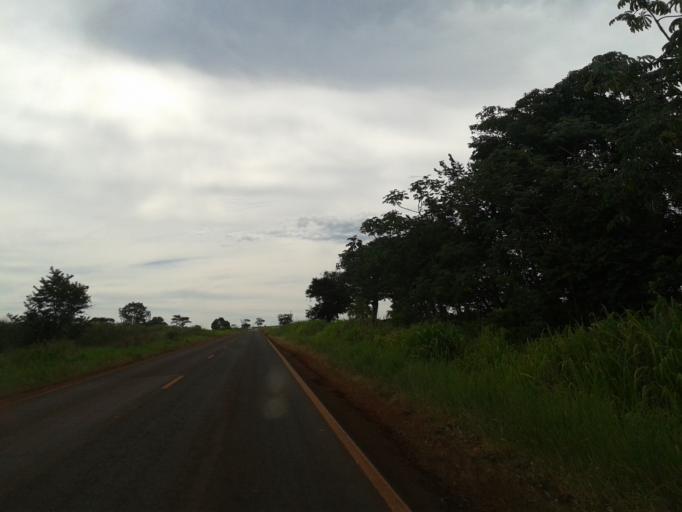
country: BR
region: Minas Gerais
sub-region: Capinopolis
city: Capinopolis
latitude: -18.6903
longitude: -49.3753
